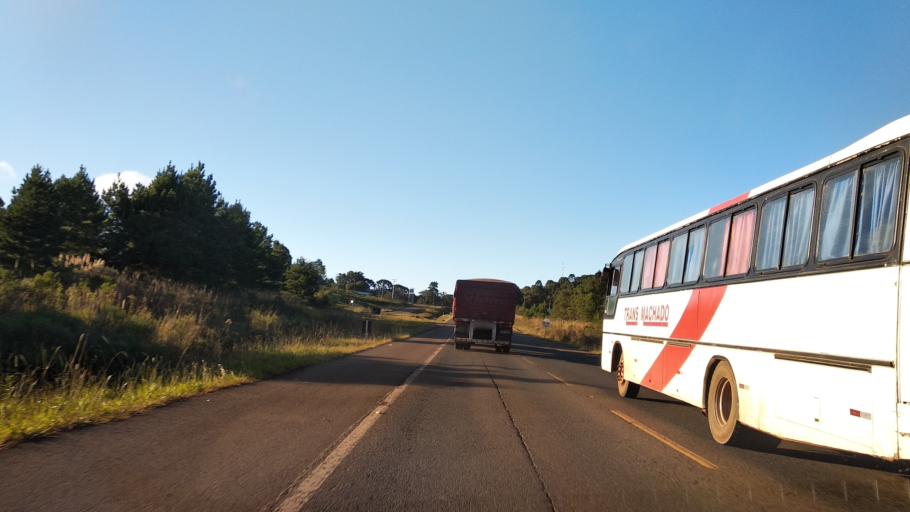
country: BR
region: Santa Catarina
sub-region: Correia Pinto
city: Correia Pinto
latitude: -27.6425
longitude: -50.5955
